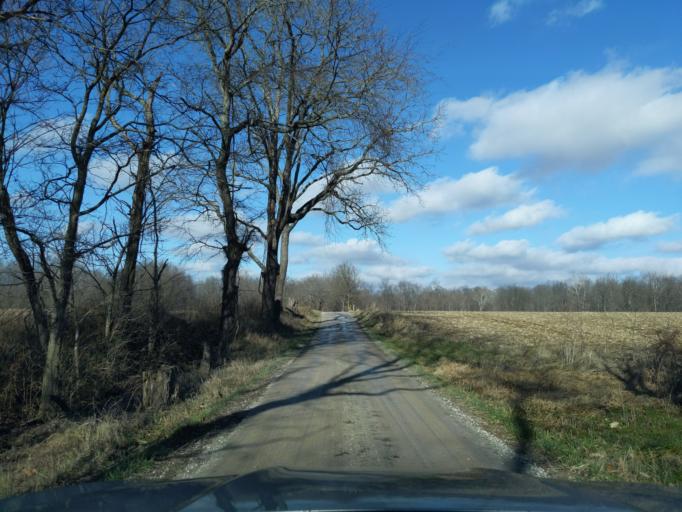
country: US
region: Indiana
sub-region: Decatur County
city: Greensburg
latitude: 39.2451
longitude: -85.4841
